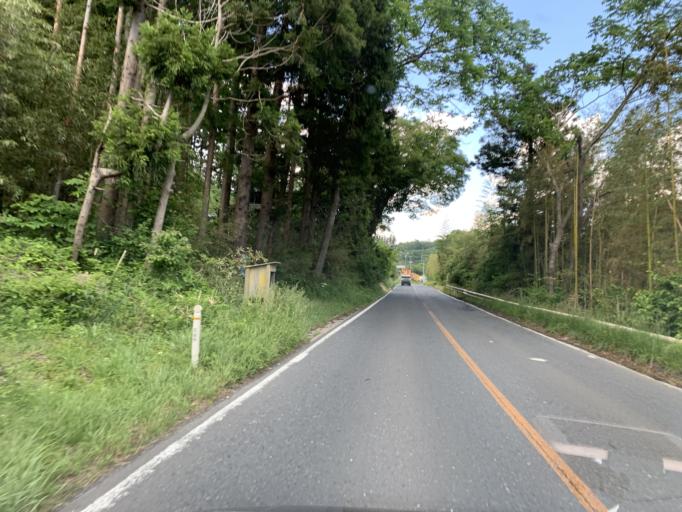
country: JP
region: Miyagi
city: Wakuya
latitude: 38.5594
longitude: 141.1359
